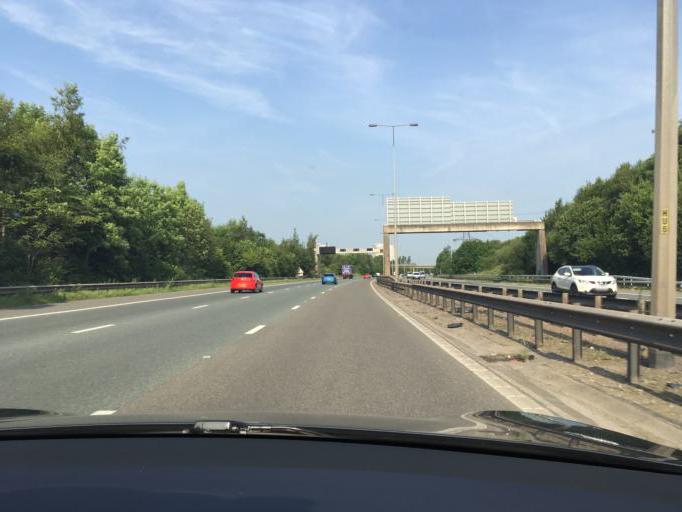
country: GB
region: England
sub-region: Manchester
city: Failsworth
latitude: 53.5276
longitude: -2.1772
